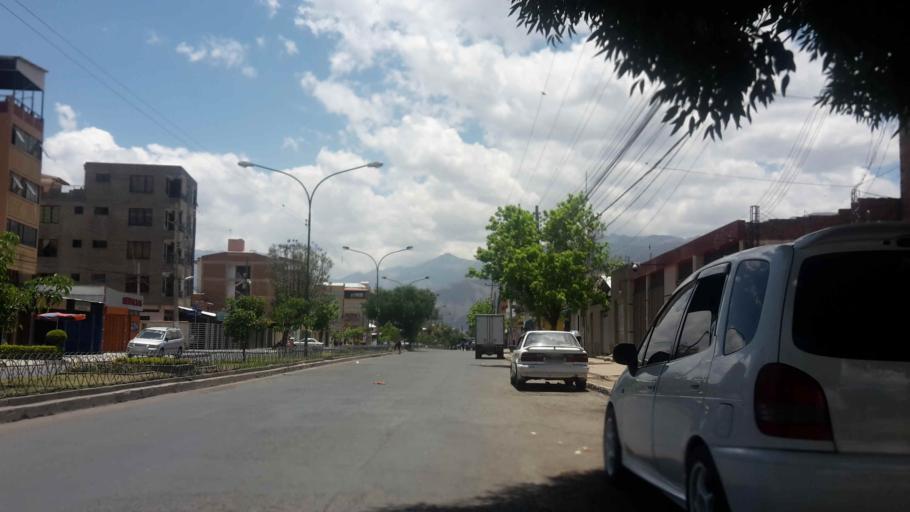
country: BO
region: Cochabamba
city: Cochabamba
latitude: -17.3564
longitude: -66.1868
